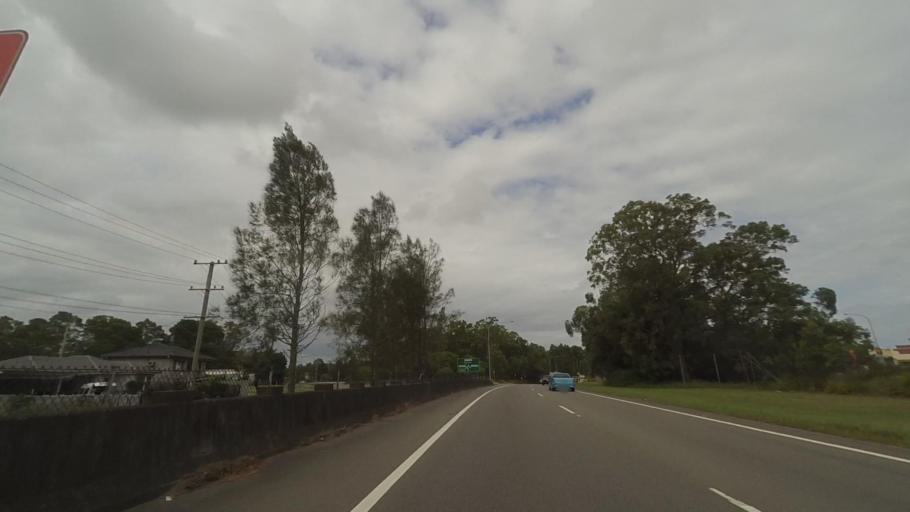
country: AU
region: New South Wales
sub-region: Port Stephens Shire
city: Raymond Terrace
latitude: -32.7824
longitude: 151.7364
